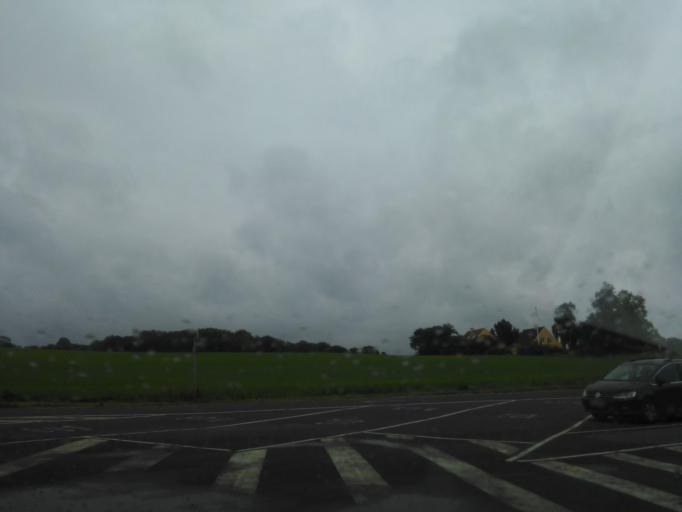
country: DK
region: Capital Region
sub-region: Bornholm Kommune
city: Ronne
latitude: 55.2308
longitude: 14.7256
